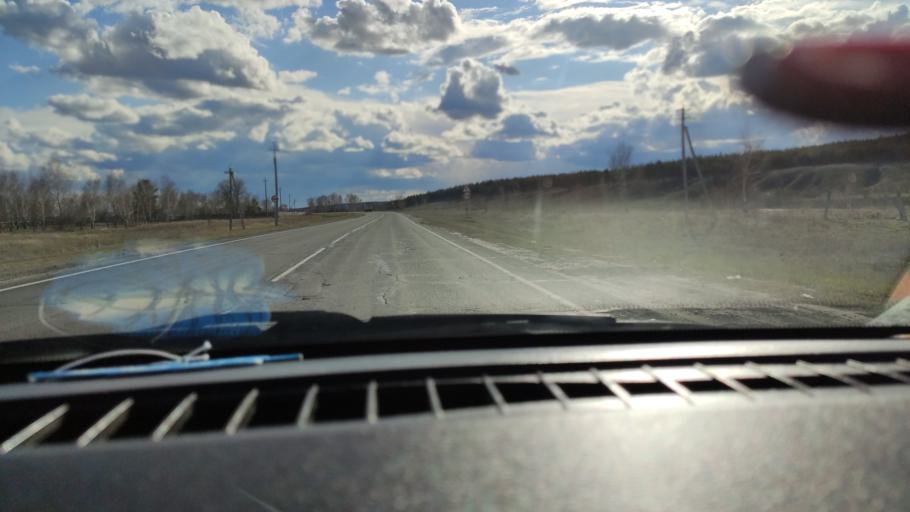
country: RU
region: Saratov
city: Sinodskoye
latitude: 52.0388
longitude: 46.7313
